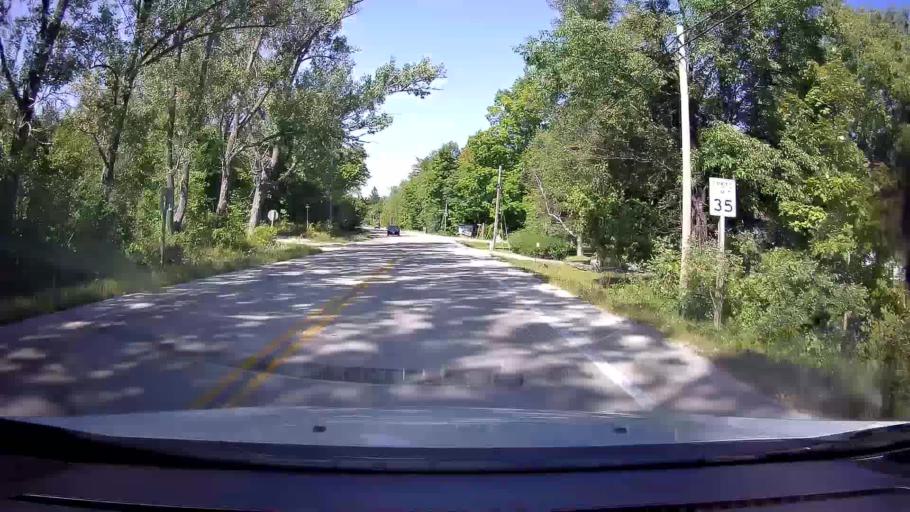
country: US
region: Michigan
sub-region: Delta County
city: Escanaba
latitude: 45.2809
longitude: -87.0194
